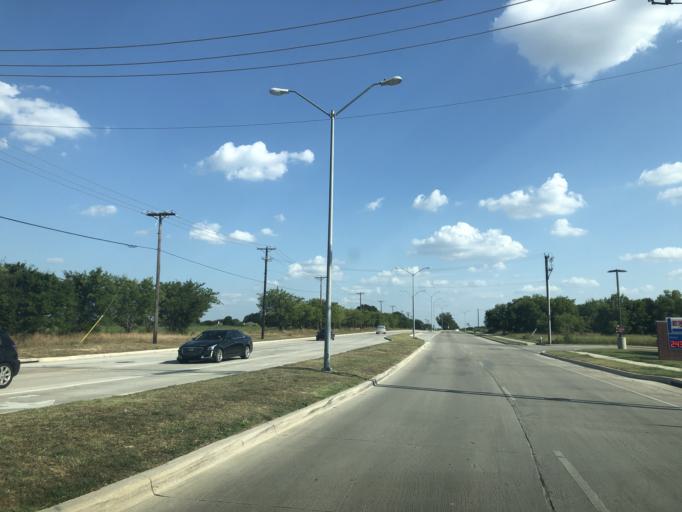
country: US
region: Texas
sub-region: Tarrant County
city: Saginaw
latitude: 32.8586
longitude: -97.3910
